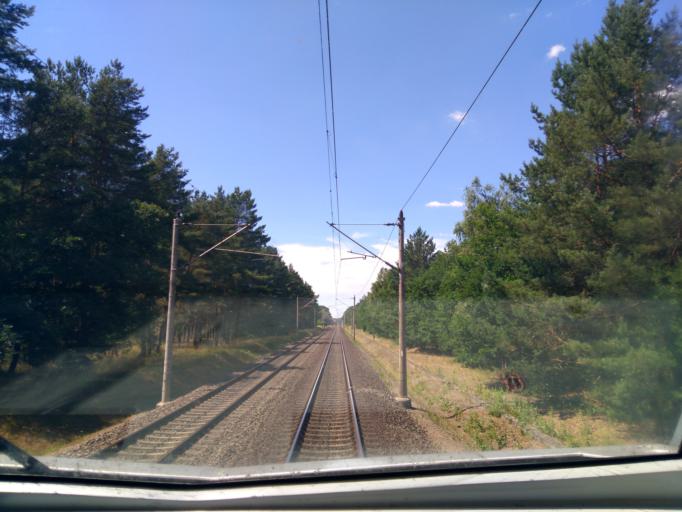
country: DE
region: Brandenburg
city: Ruhstadt
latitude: 52.9806
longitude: 11.8854
